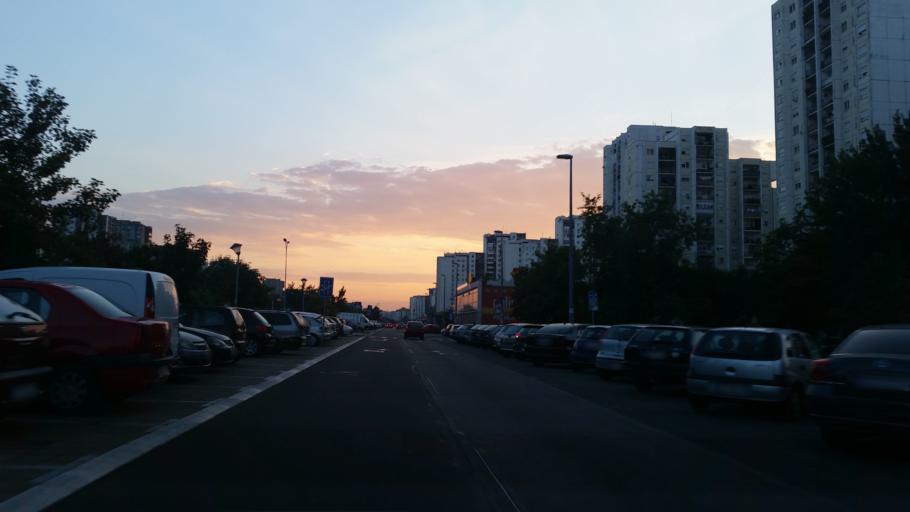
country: RS
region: Central Serbia
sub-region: Belgrade
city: Zemun
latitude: 44.8063
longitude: 20.3811
